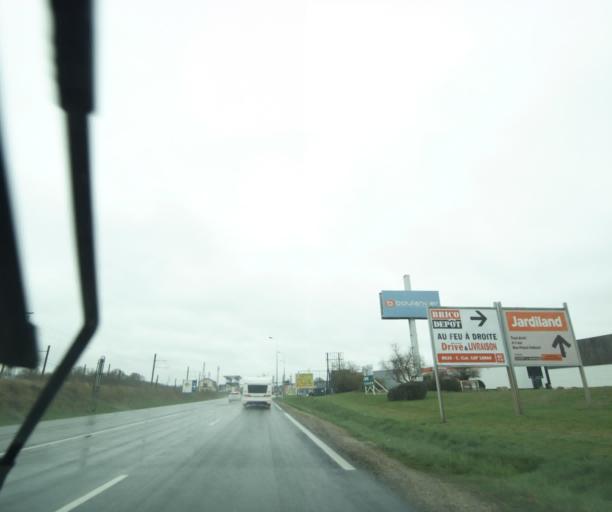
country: FR
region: Centre
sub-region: Departement du Loiret
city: Saran
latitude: 47.9663
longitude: 1.8878
